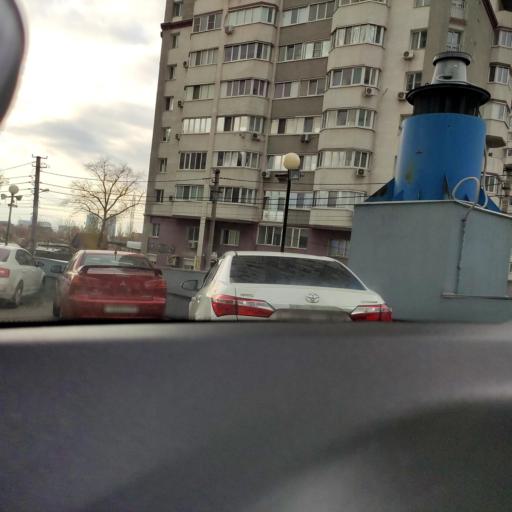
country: RU
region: Samara
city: Samara
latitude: 53.2212
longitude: 50.1938
